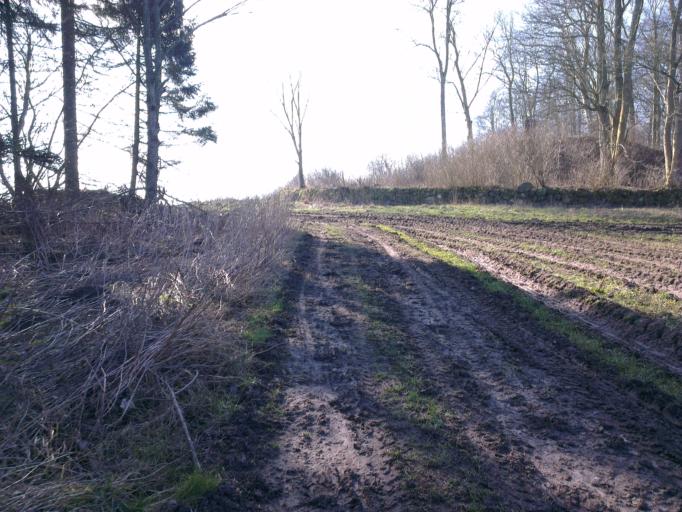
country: DK
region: Capital Region
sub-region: Frederikssund Kommune
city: Skibby
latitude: 55.7820
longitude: 11.9566
